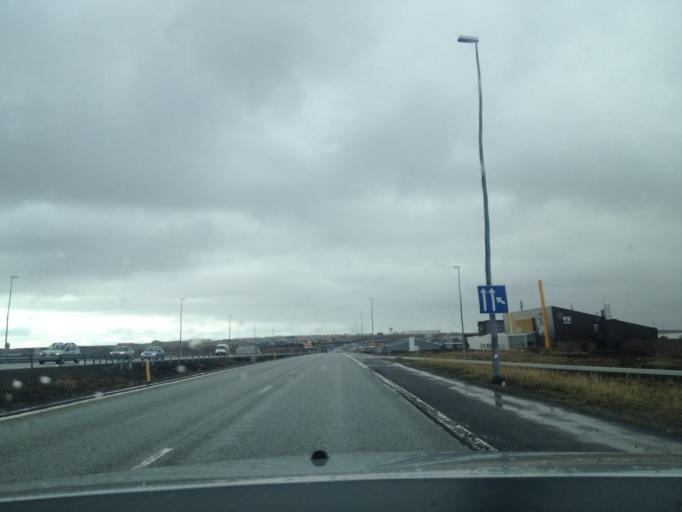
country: IS
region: Southern Peninsula
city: Reykjanesbaer
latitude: 63.9693
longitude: -22.5138
